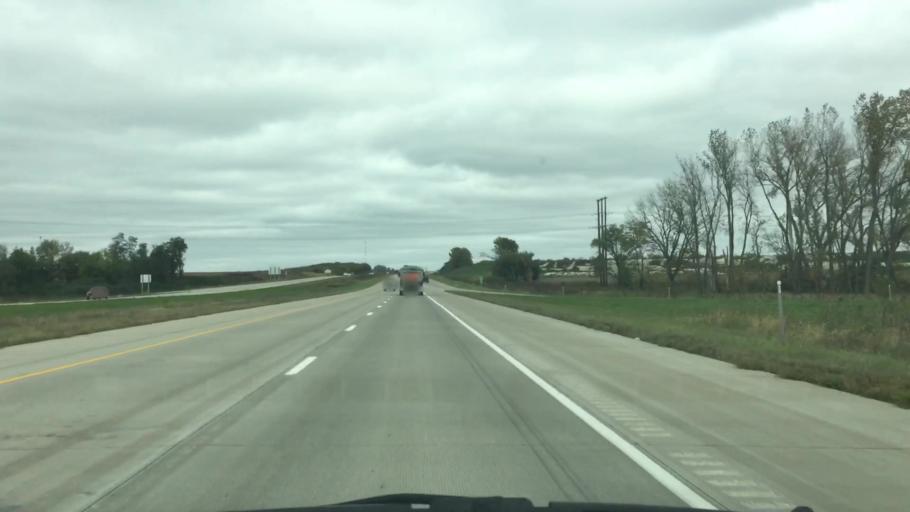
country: US
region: Iowa
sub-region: Warren County
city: Norwalk
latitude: 41.3652
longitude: -93.7798
